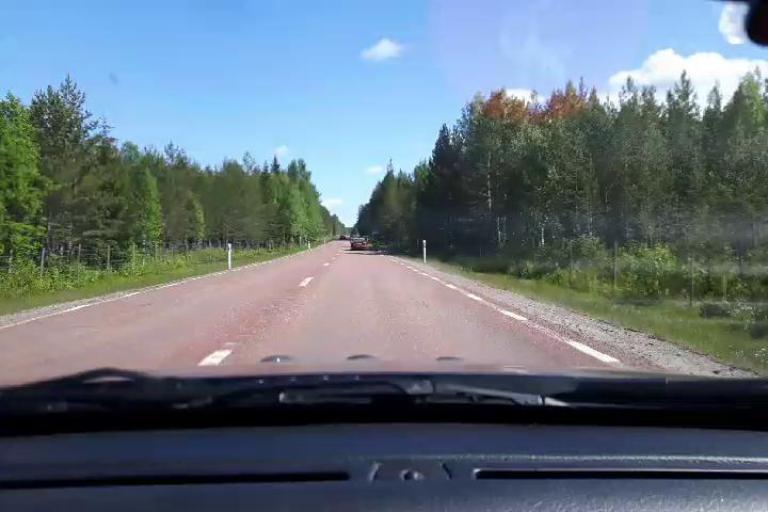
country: SE
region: Gaevleborg
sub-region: Hudiksvalls Kommun
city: Delsbo
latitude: 61.7921
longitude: 16.5875
